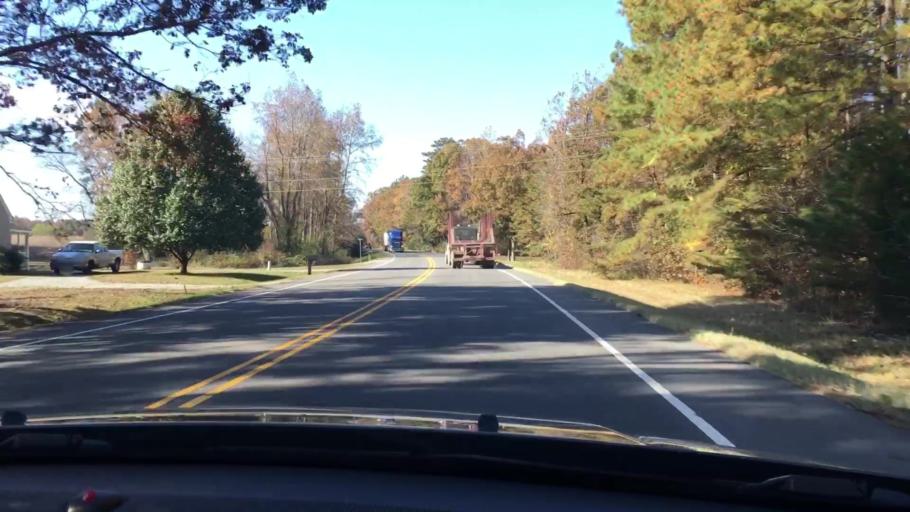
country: US
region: Virginia
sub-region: King William County
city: Central Garage
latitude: 37.7740
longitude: -77.1577
